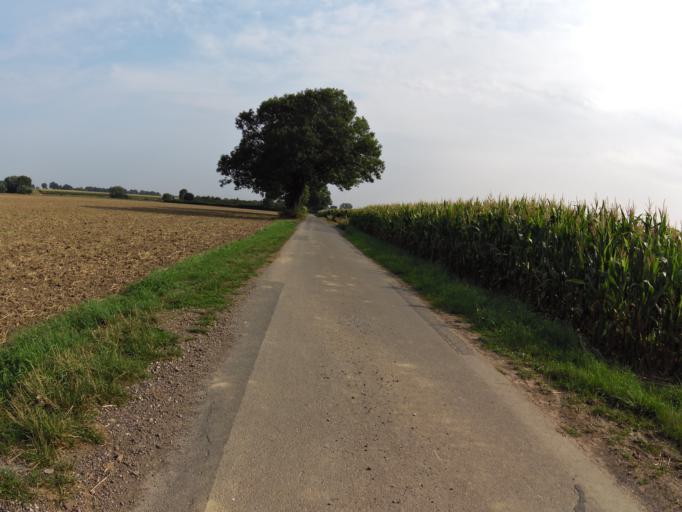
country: DE
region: Lower Saxony
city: Raddestorf
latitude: 52.4775
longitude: 9.0137
